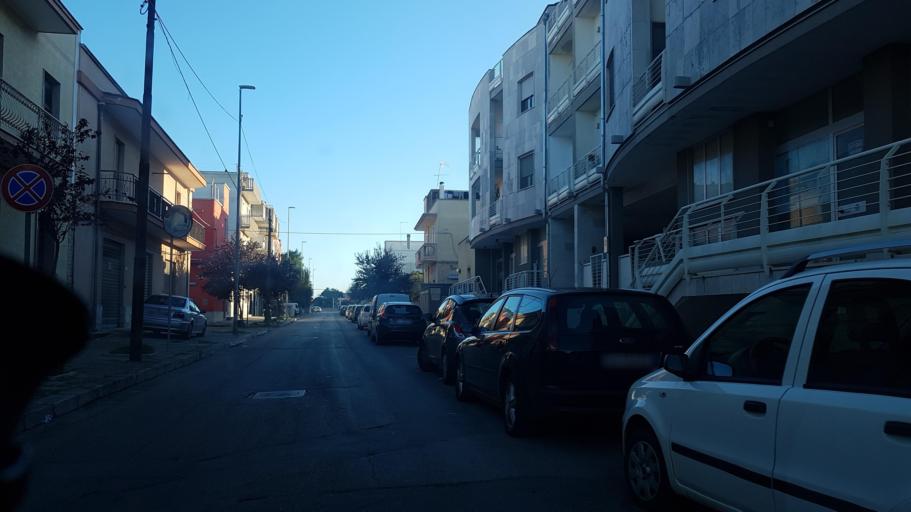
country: IT
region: Apulia
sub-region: Provincia di Brindisi
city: Latiano
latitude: 40.5491
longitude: 17.7189
